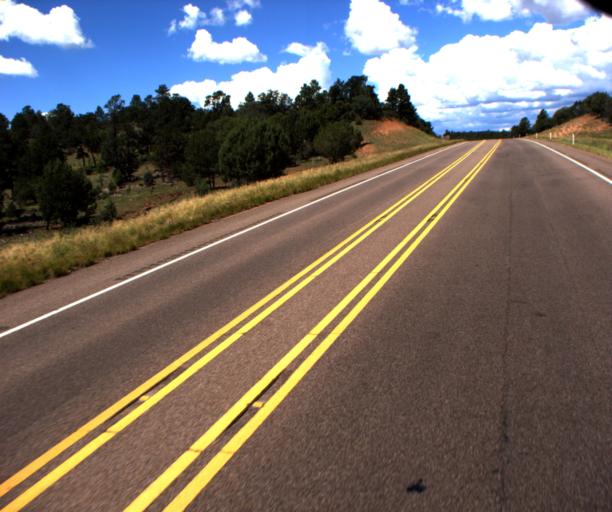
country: US
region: Arizona
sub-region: Navajo County
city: Heber-Overgaard
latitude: 34.3668
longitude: -110.3637
